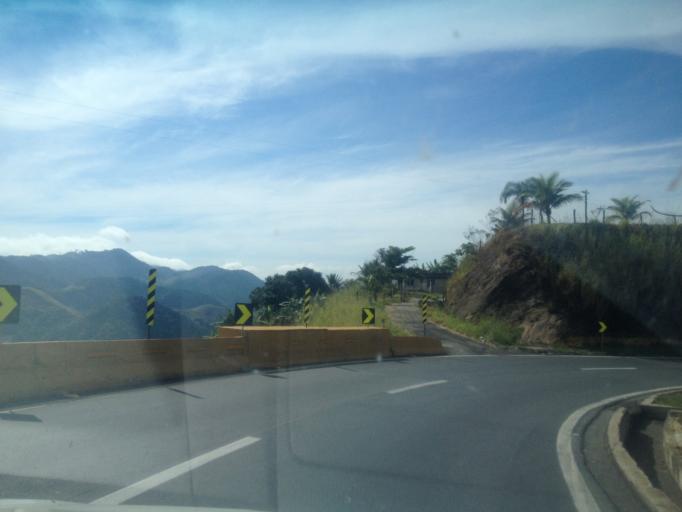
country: BR
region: Rio de Janeiro
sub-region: Pirai
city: Pirai
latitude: -22.6691
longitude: -43.8361
